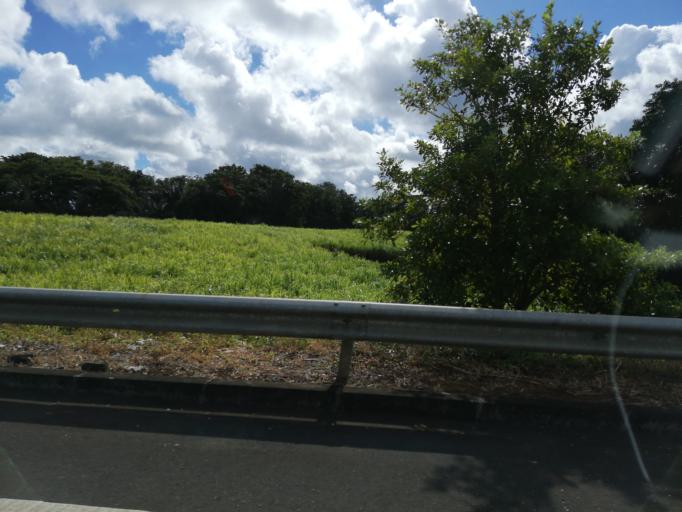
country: MU
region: Grand Port
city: Plaine Magnien
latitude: -20.4075
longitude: 57.6742
